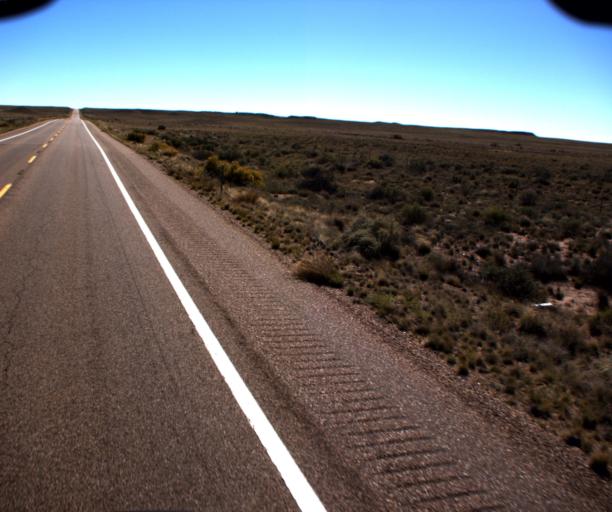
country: US
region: Arizona
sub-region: Navajo County
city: Holbrook
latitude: 34.7826
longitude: -109.8571
